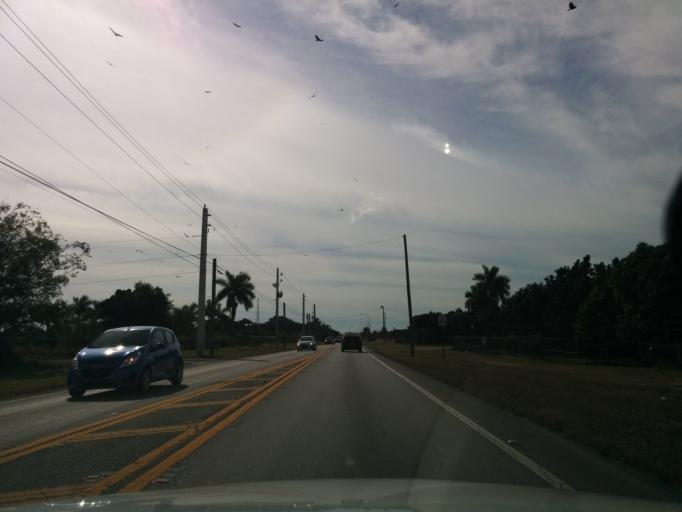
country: US
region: Florida
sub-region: Miami-Dade County
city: Naranja
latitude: 25.5342
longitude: -80.4780
